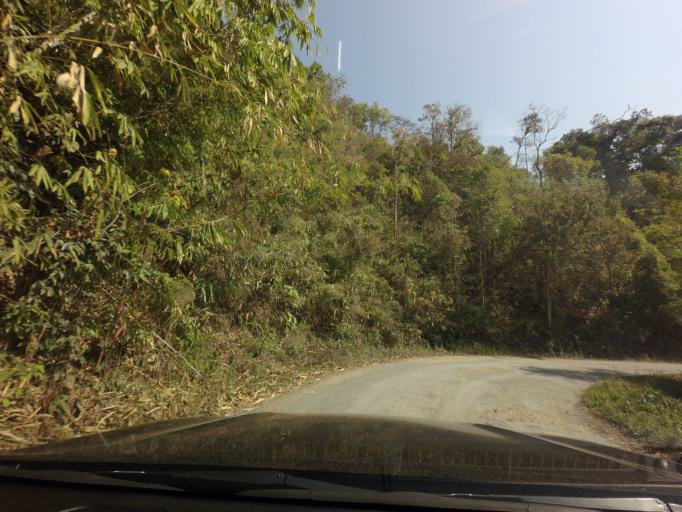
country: TH
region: Kanchanaburi
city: Thong Pha Phum
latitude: 14.6952
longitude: 98.4577
